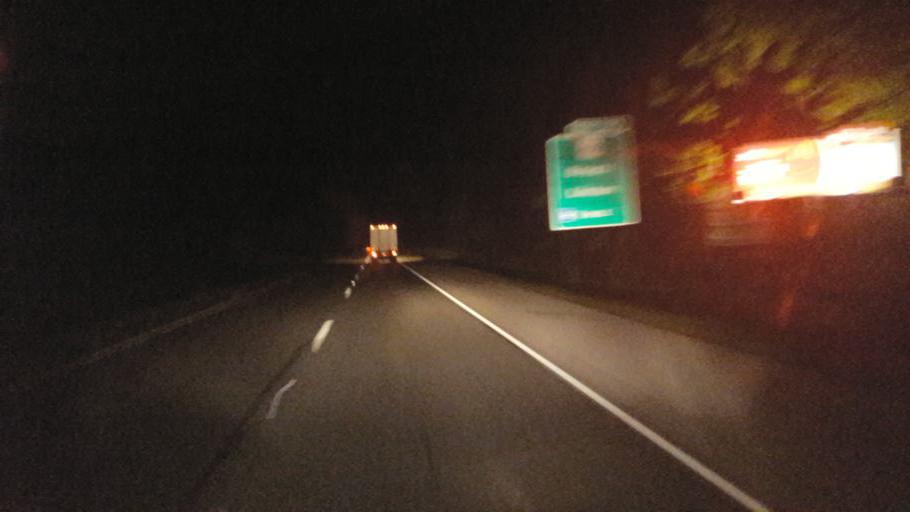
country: US
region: Indiana
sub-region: Clay County
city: Brazil
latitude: 39.4544
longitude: -87.1013
